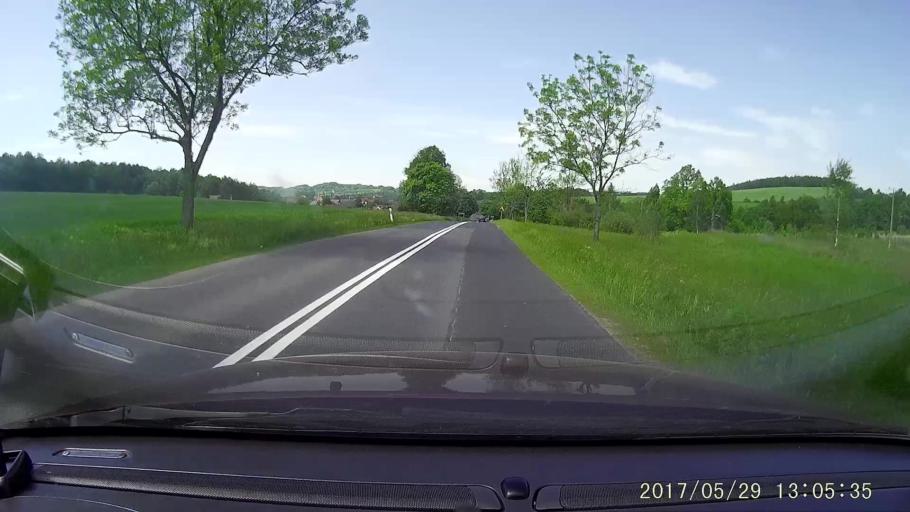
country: PL
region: Lower Silesian Voivodeship
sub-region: Powiat jeleniogorski
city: Stara Kamienica
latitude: 50.9454
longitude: 15.5886
